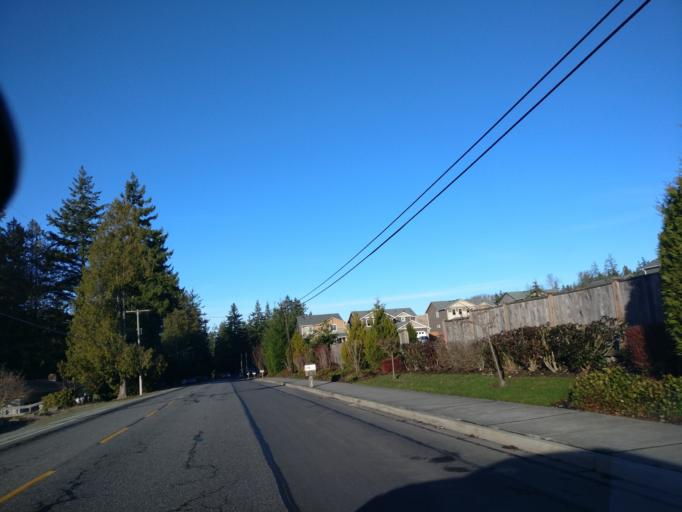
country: US
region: Washington
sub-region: Skagit County
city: Mount Vernon
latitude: 48.4184
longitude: -122.2970
